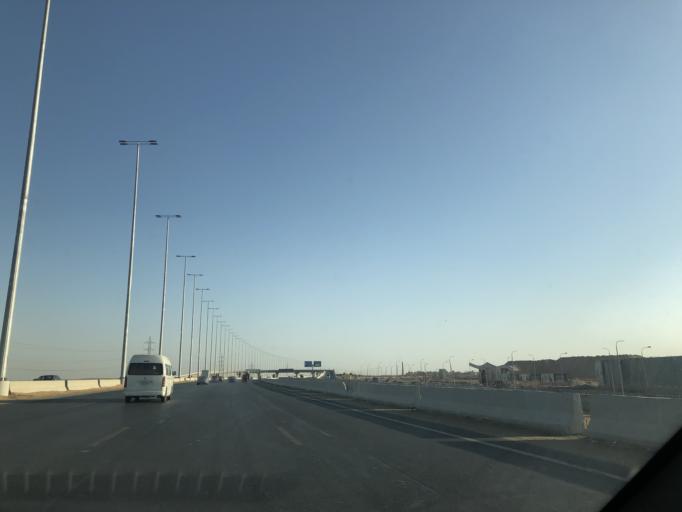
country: EG
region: Al Jizah
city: Madinat Sittah Uktubar
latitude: 29.9332
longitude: 31.0971
